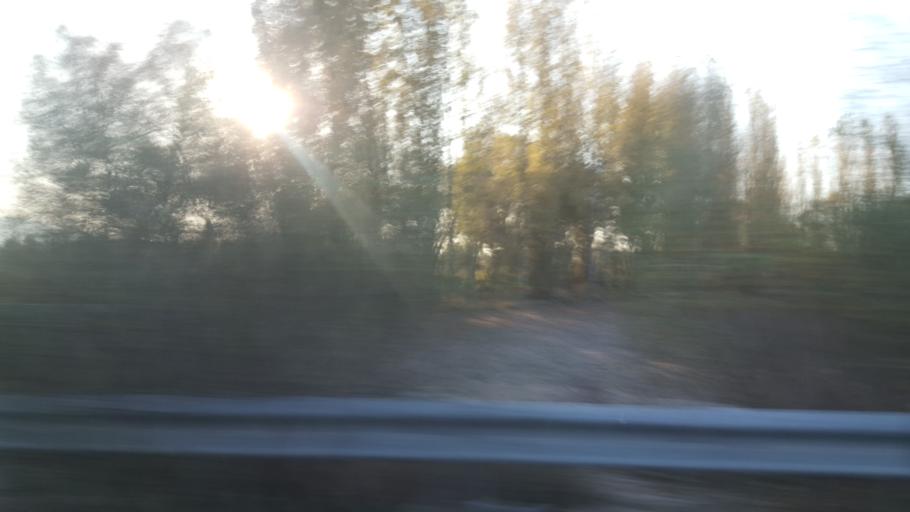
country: TR
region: Eskisehir
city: Mahmudiye
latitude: 39.5732
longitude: 30.9117
